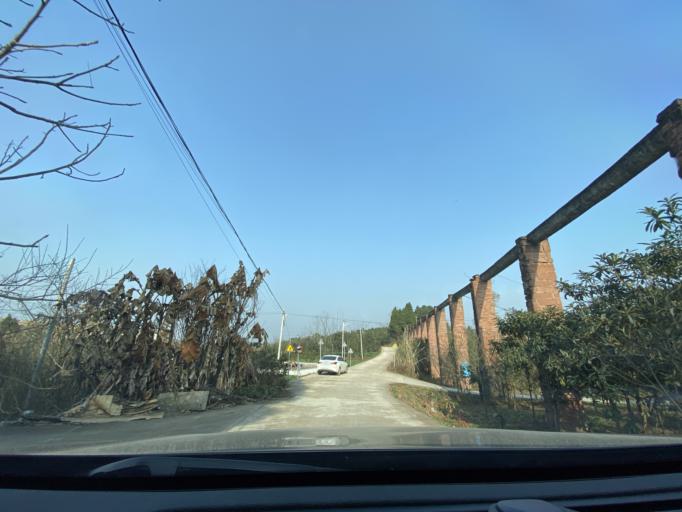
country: CN
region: Sichuan
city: Wenlin
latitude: 30.2495
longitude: 104.2497
